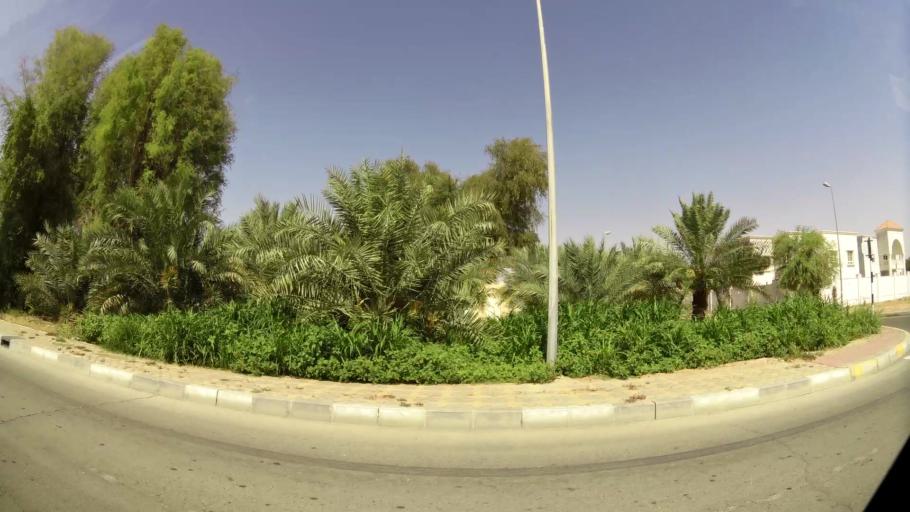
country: OM
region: Al Buraimi
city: Al Buraymi
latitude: 24.3000
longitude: 55.7802
